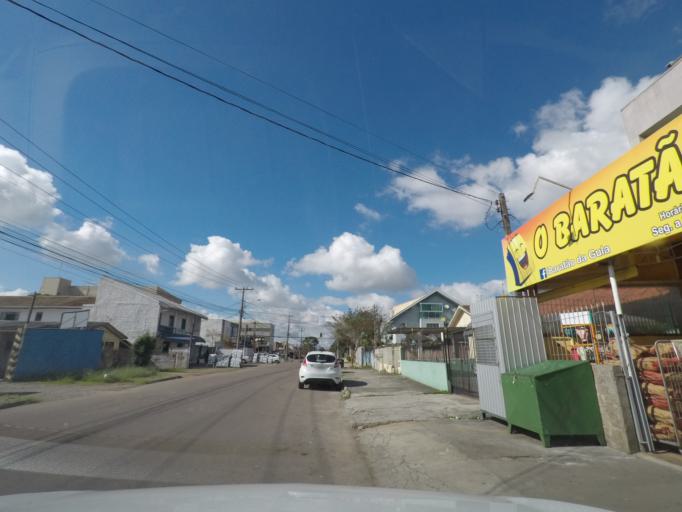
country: BR
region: Parana
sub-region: Curitiba
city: Curitiba
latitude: -25.4761
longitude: -49.2412
